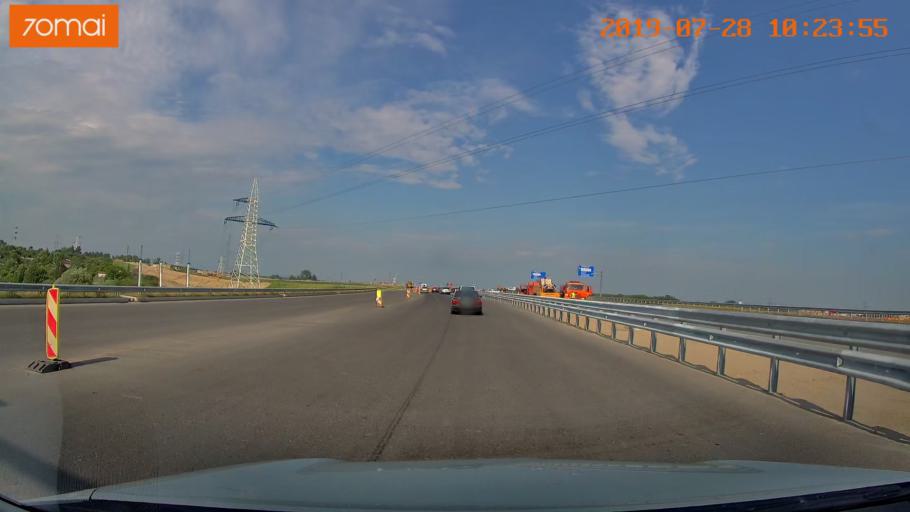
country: RU
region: Kaliningrad
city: Maloye Isakovo
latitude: 54.7677
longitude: 20.5546
